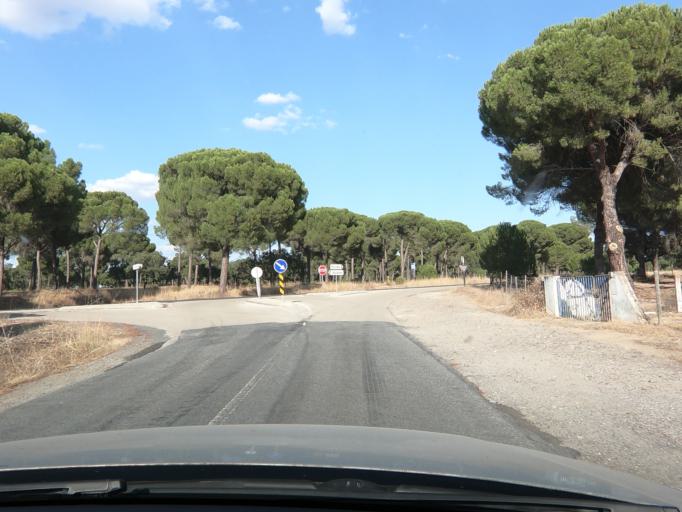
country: PT
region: Setubal
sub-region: Alcacer do Sal
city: Alcacer do Sal
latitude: 38.2652
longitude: -8.3470
